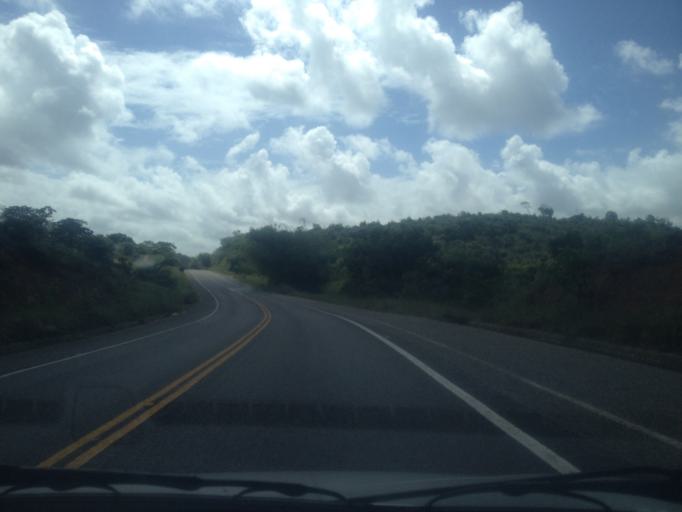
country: BR
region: Bahia
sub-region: Conde
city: Conde
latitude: -12.0470
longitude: -37.7064
